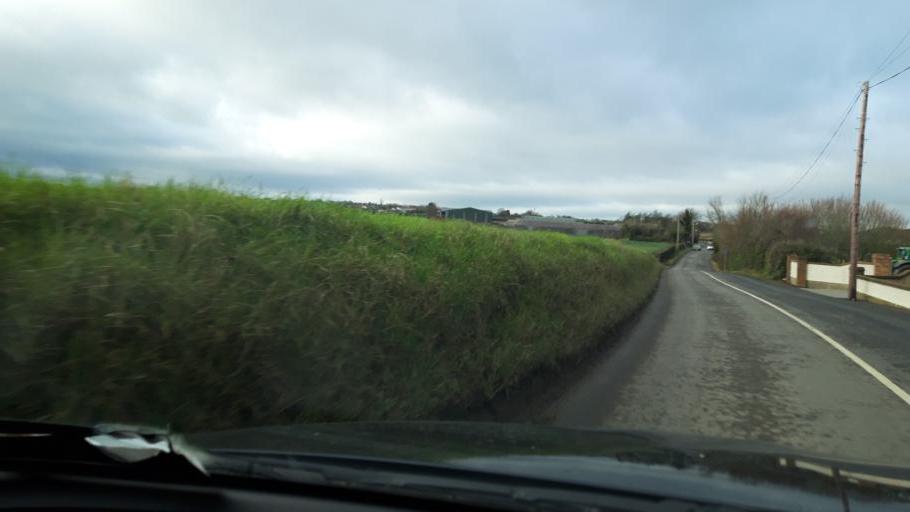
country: IE
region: Leinster
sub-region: Fingal County
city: Skerries
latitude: 53.5573
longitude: -6.1353
